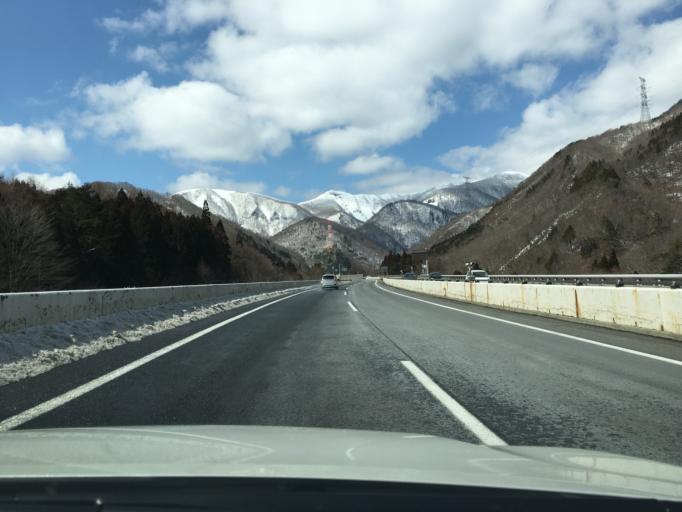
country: JP
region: Yamagata
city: Yamagata-shi
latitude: 38.2248
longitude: 140.5030
